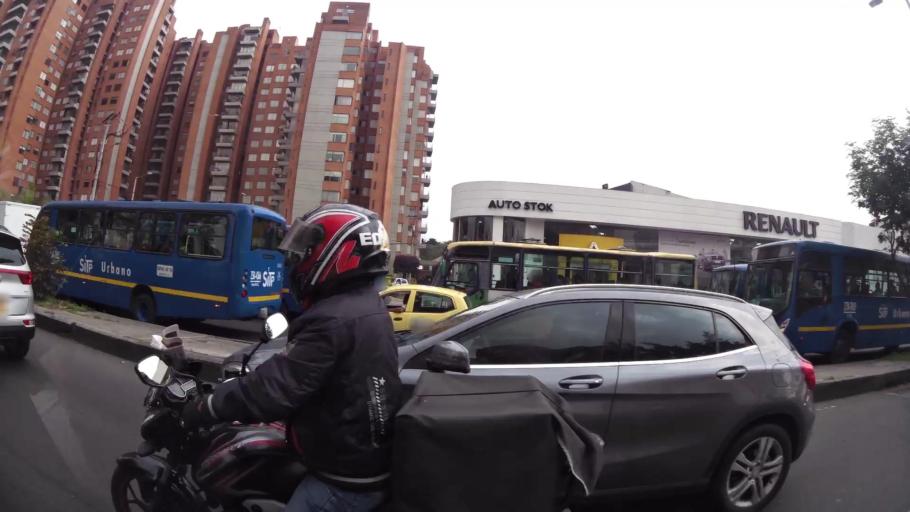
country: CO
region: Bogota D.C.
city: Barrio San Luis
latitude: 4.6900
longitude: -74.0692
